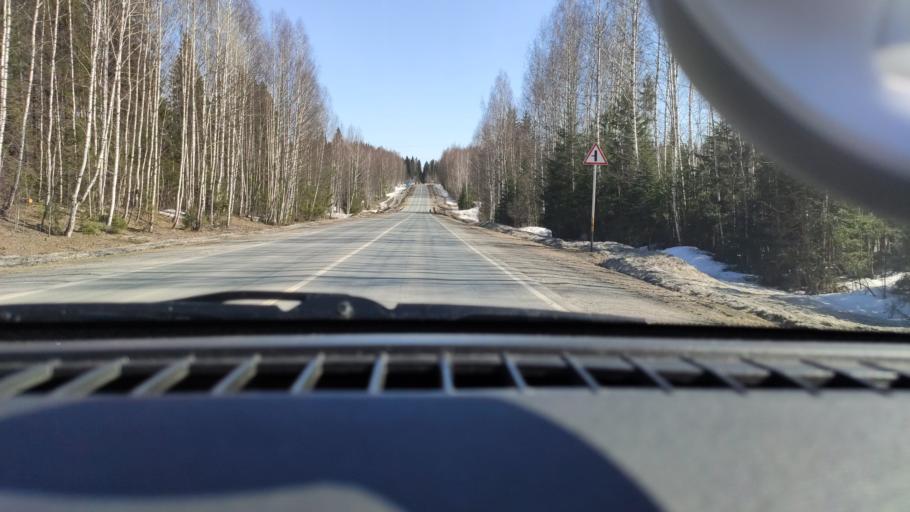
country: RU
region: Perm
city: Perm
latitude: 58.1363
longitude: 56.2921
